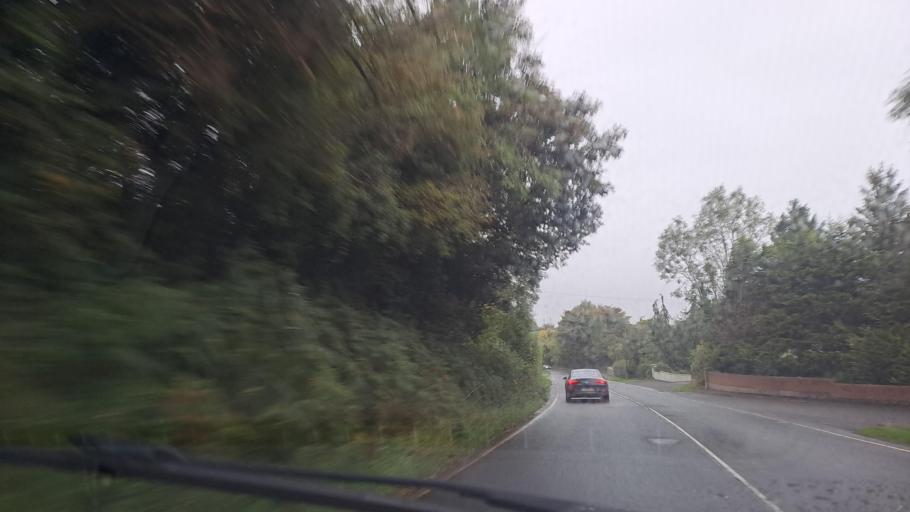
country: IE
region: Ulster
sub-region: County Monaghan
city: Monaghan
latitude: 54.2300
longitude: -6.9571
